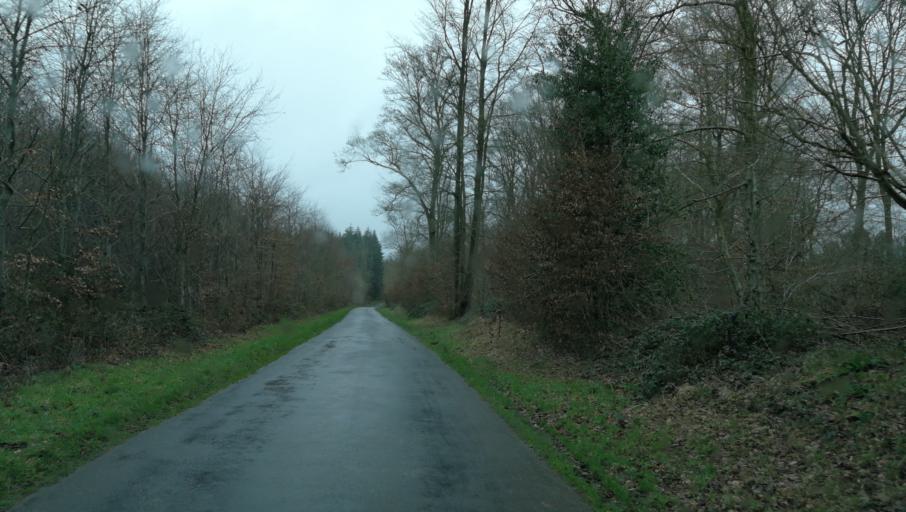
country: FR
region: Haute-Normandie
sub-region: Departement de l'Eure
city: Brionne
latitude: 49.1808
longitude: 0.6964
